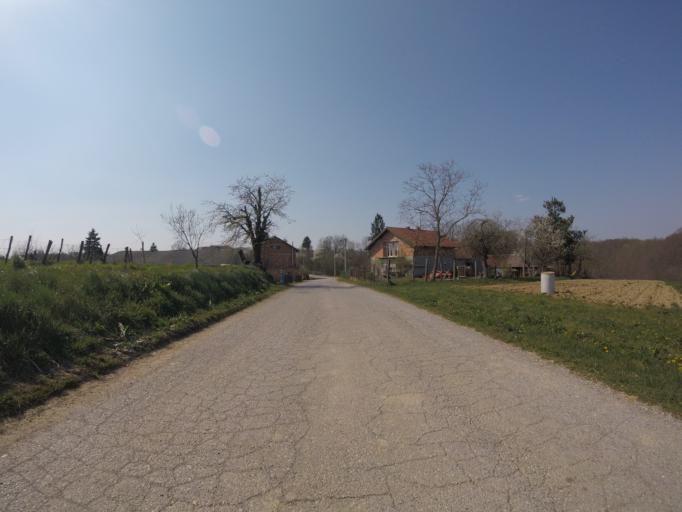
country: HR
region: Grad Zagreb
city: Strmec
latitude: 45.5595
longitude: 15.9104
